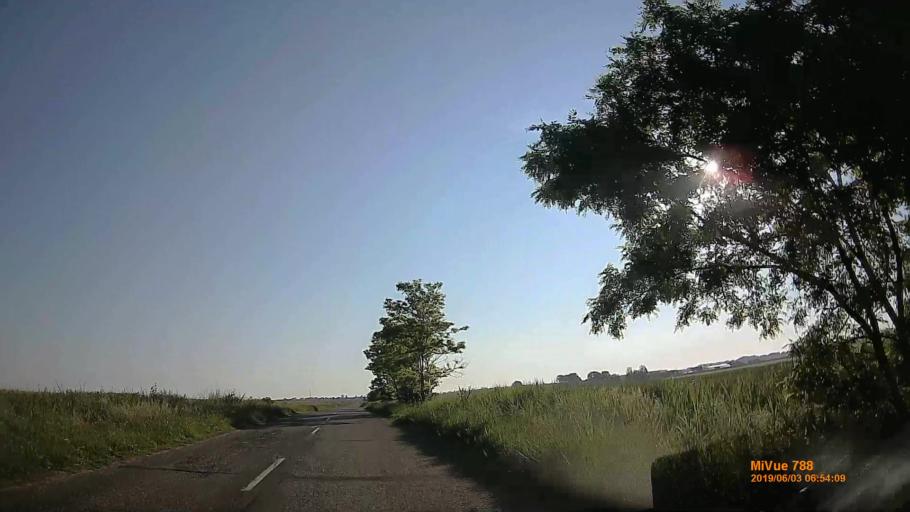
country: HU
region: Pest
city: Bugyi
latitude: 47.2118
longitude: 19.2226
